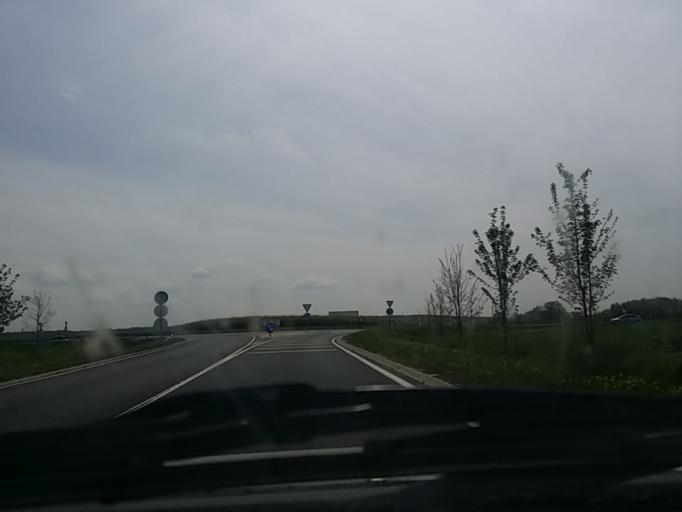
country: HU
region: Zala
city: Nagykanizsa
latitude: 46.4699
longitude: 17.0346
